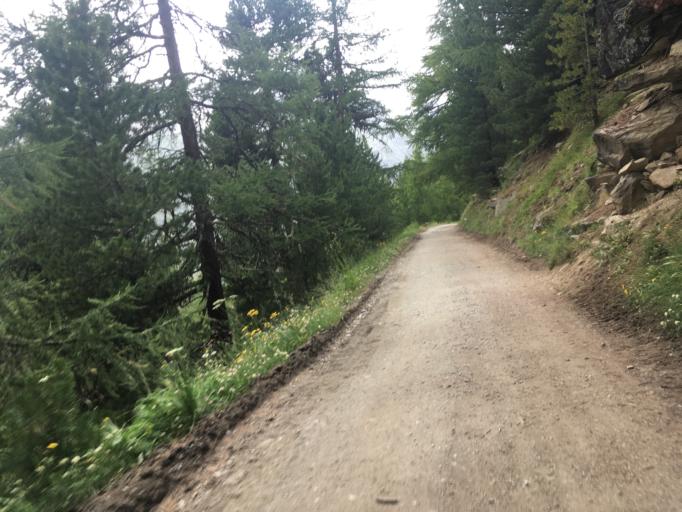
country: CH
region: Valais
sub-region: Visp District
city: Zermatt
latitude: 46.0259
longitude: 7.7763
